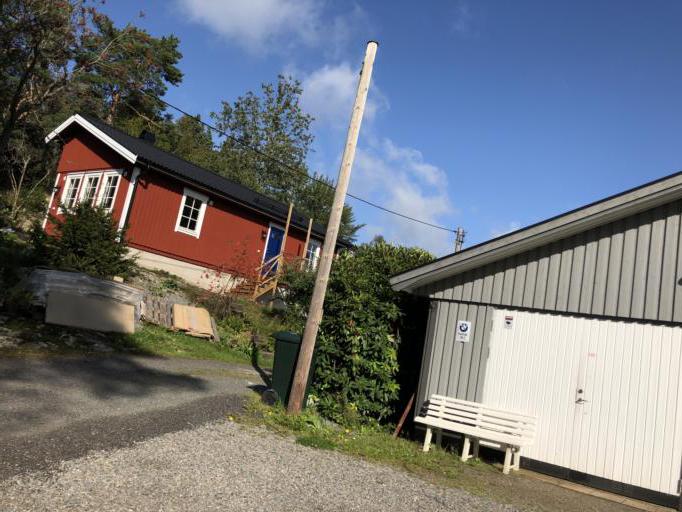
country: SE
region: Vaestra Goetaland
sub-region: Goteborg
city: Torslanda
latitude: 57.7352
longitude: 11.8470
